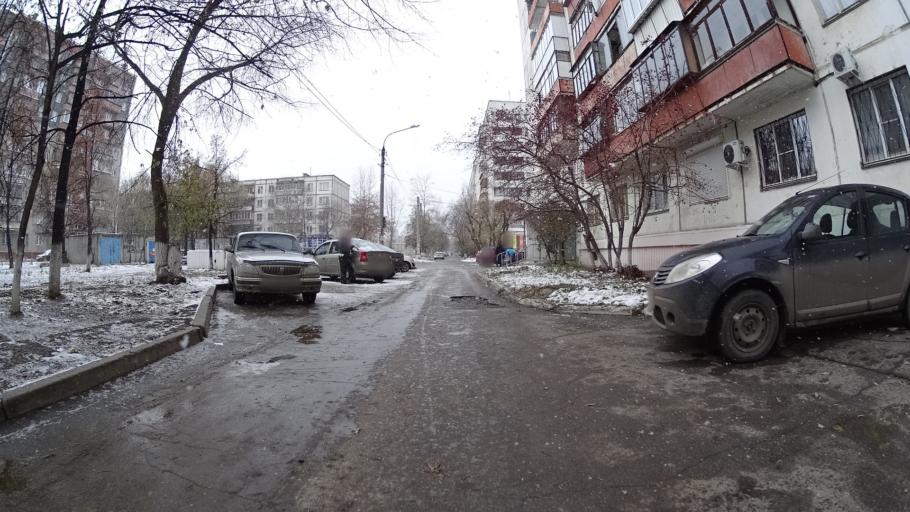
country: RU
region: Chelyabinsk
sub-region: Gorod Chelyabinsk
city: Chelyabinsk
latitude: 55.1940
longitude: 61.3150
